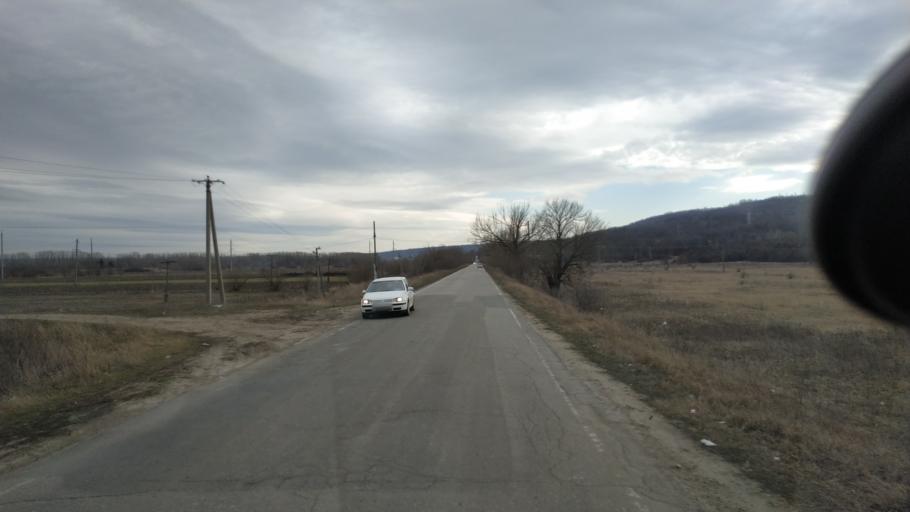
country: MD
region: Chisinau
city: Vadul lui Voda
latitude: 47.1152
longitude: 29.0575
